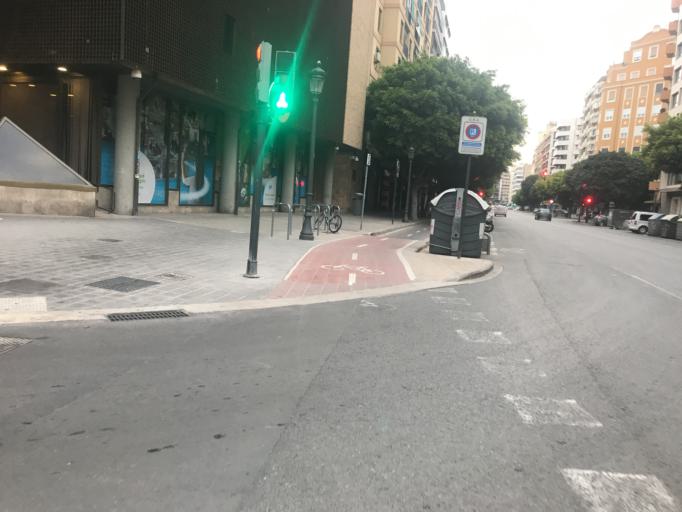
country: ES
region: Valencia
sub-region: Provincia de Valencia
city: Valencia
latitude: 39.4621
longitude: -0.3823
